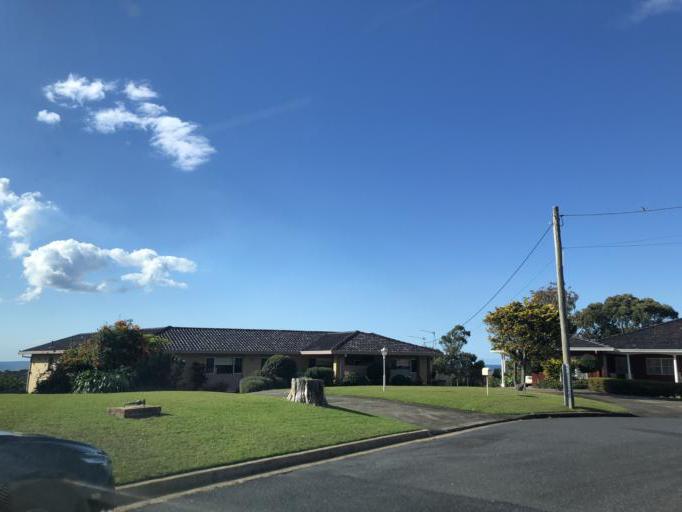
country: AU
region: New South Wales
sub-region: Coffs Harbour
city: Coffs Harbour
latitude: -30.2768
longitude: 153.1354
